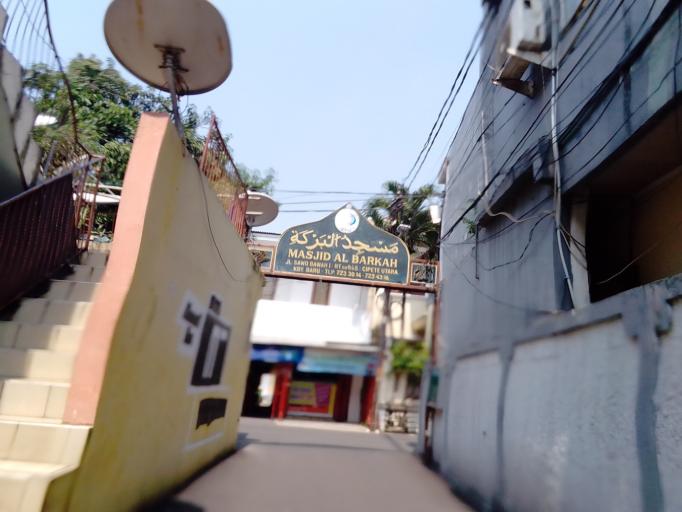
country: ID
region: Jakarta Raya
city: Jakarta
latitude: -6.2620
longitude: 106.7978
